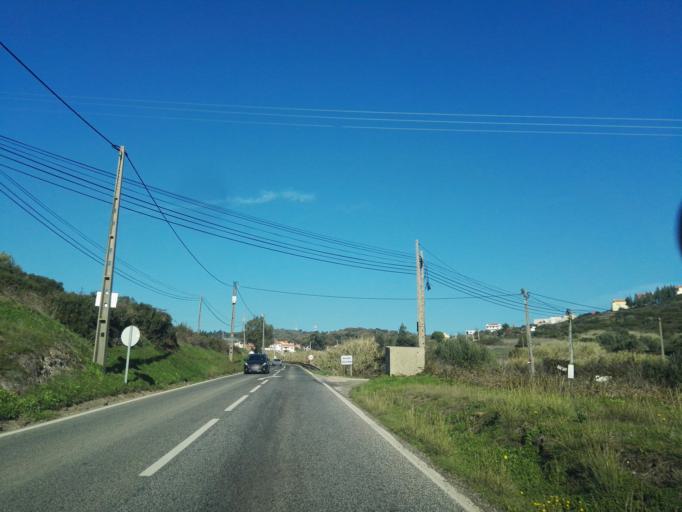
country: PT
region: Lisbon
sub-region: Loures
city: Loures
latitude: 38.8631
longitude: -9.1817
